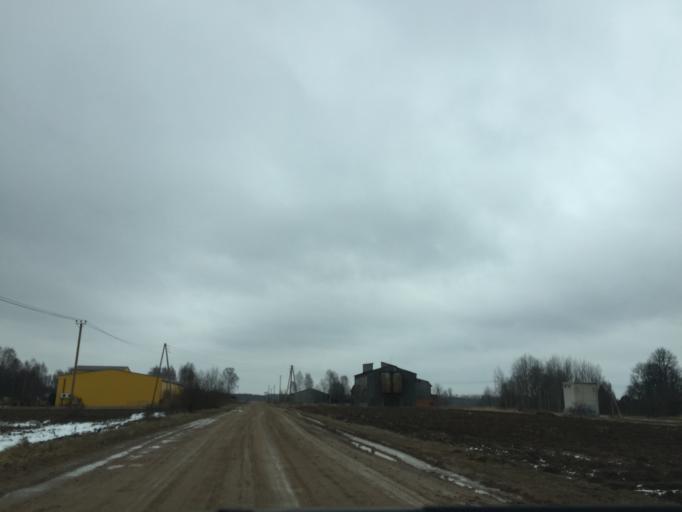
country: LV
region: Lielvarde
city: Lielvarde
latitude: 56.7573
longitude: 24.7924
